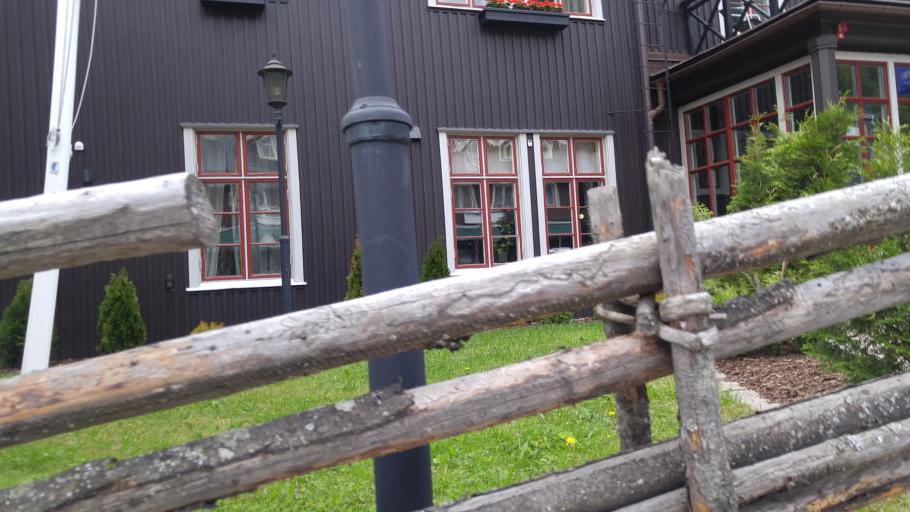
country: SE
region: Jaemtland
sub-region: Are Kommun
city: Are
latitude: 63.3996
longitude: 13.0797
